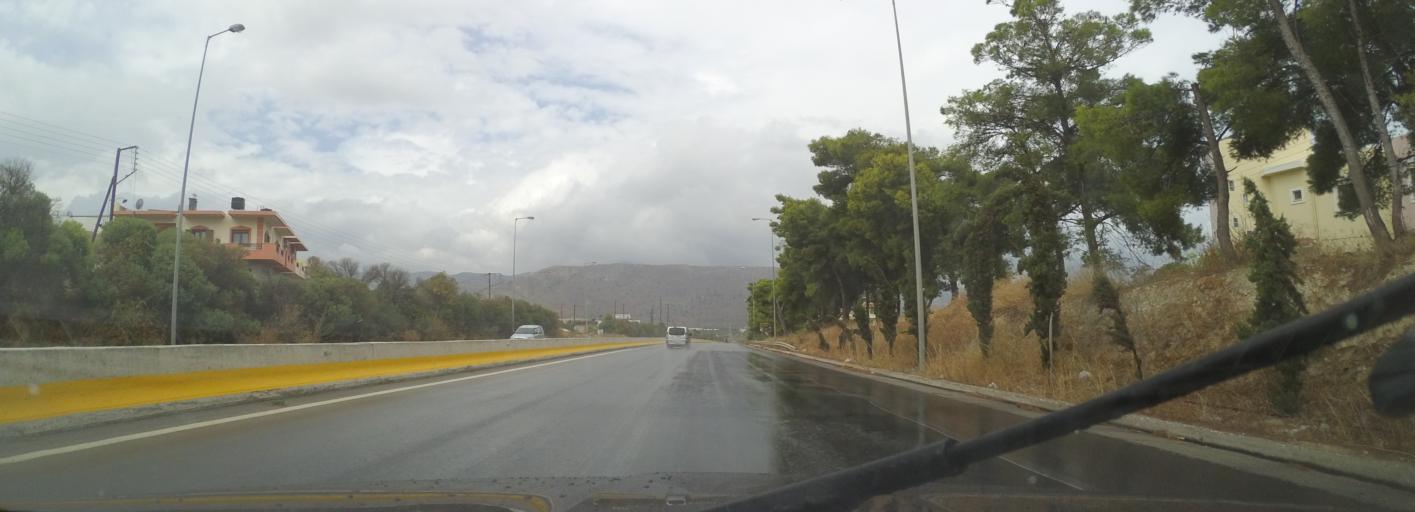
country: GR
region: Crete
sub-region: Nomos Irakleiou
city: Gazi
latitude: 35.3185
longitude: 25.0701
